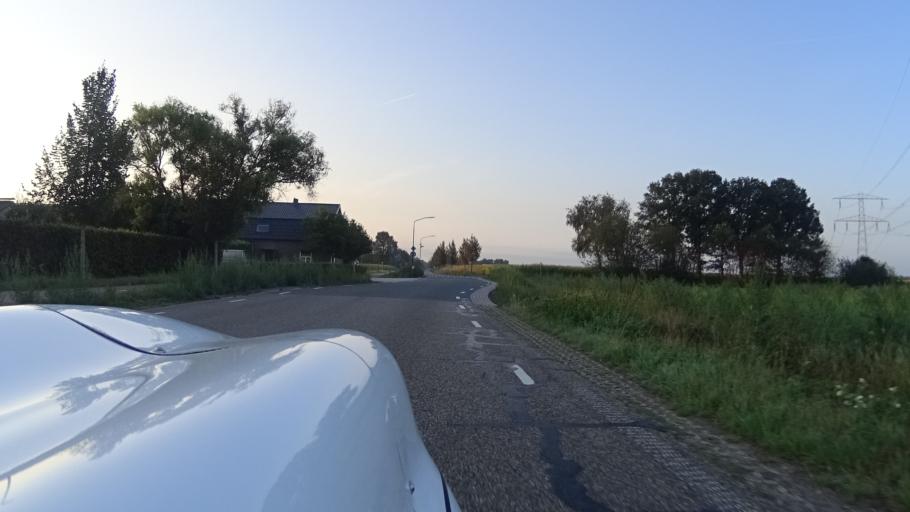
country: NL
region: North Brabant
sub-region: Gemeente Sint Anthonis
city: Sint Anthonis
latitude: 51.6127
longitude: 5.9059
